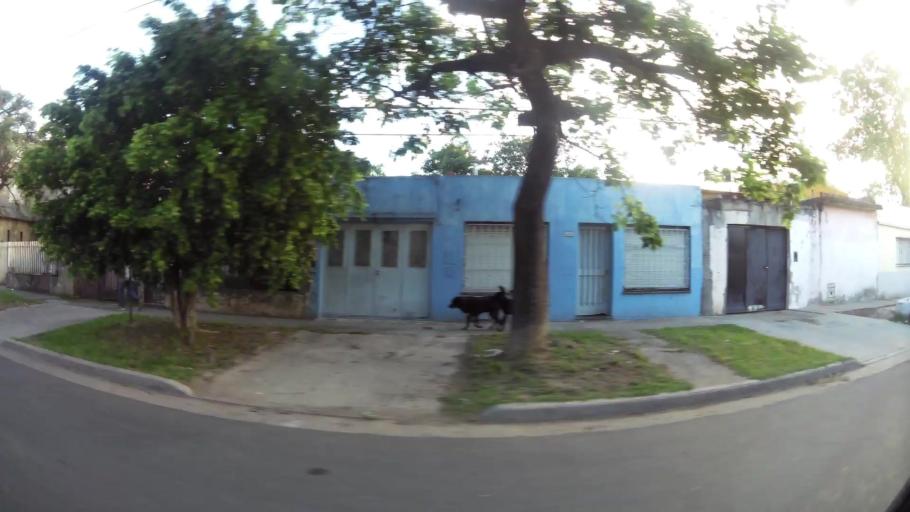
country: AR
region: Santa Fe
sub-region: Departamento de Rosario
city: Rosario
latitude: -32.9804
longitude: -60.6665
